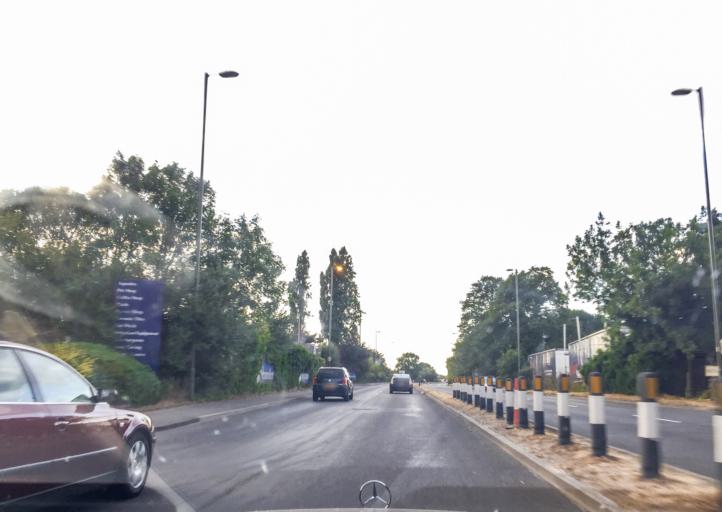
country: GB
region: England
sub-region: Surrey
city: Staines
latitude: 51.4595
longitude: -0.4939
